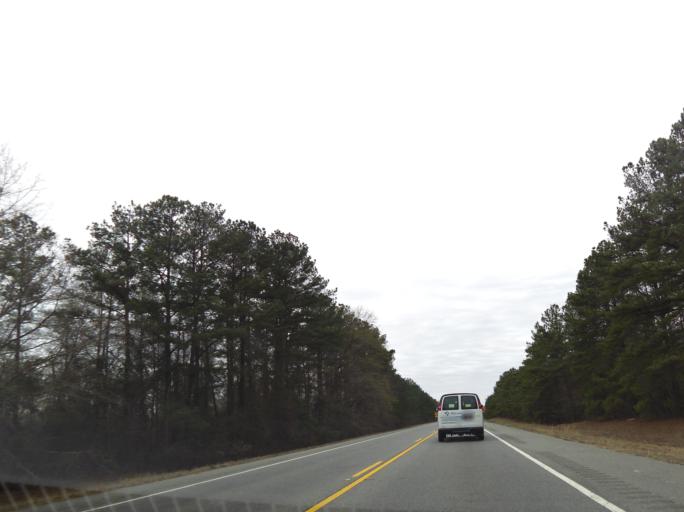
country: US
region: Georgia
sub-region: Bibb County
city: West Point
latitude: 32.7993
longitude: -83.7895
